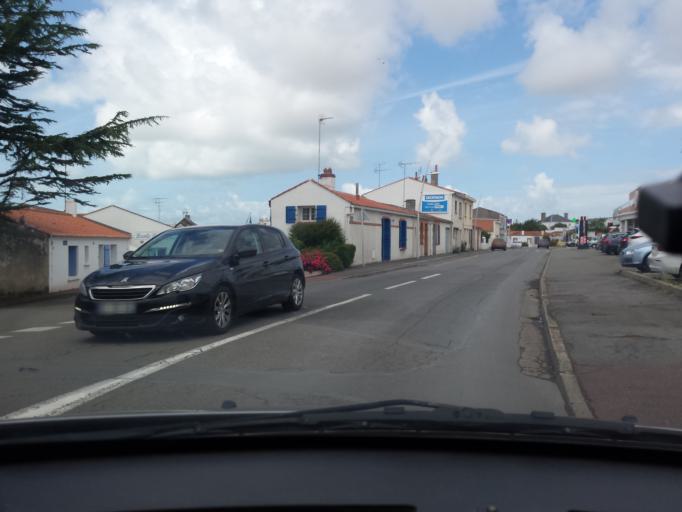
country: FR
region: Pays de la Loire
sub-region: Departement de la Vendee
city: Saint-Hilaire-de-Riez
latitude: 46.6955
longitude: -1.9261
